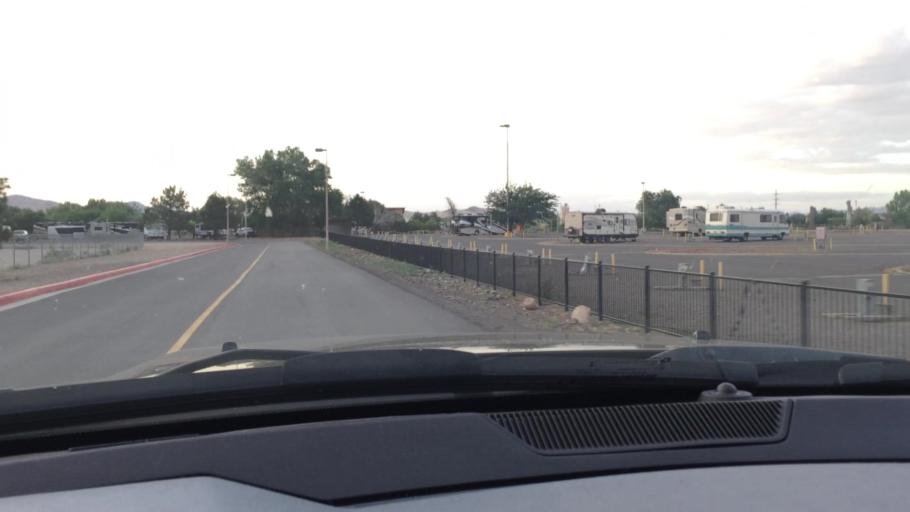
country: US
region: Nevada
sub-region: Washoe County
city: Sparks
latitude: 39.5206
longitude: -119.7741
